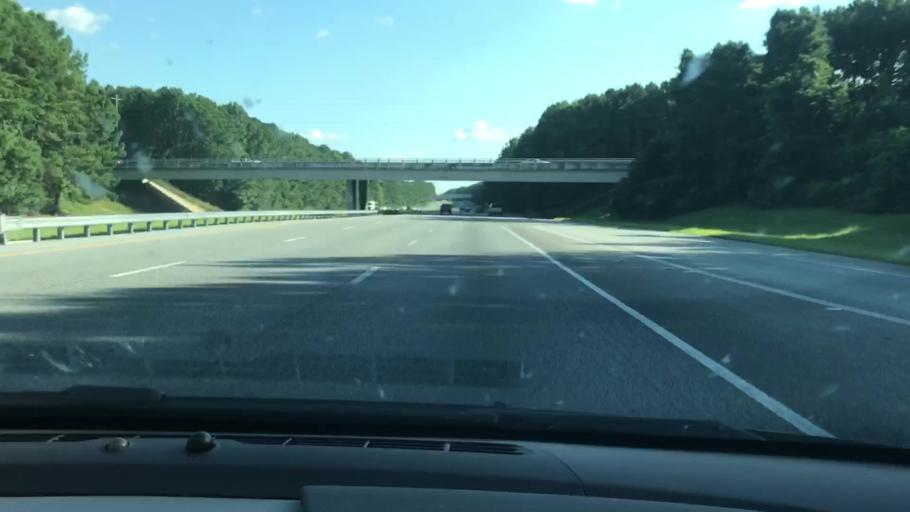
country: US
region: Alabama
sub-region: Russell County
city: Phenix City
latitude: 32.5680
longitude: -84.9623
